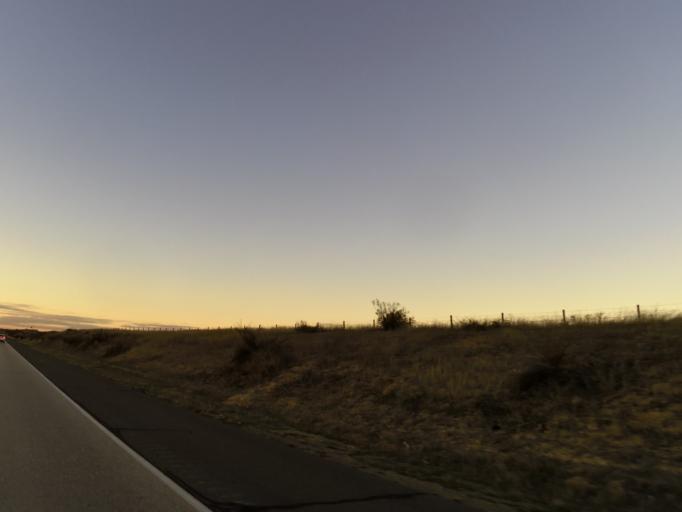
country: US
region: California
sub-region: Monterey County
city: King City
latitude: 36.0356
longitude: -120.9477
